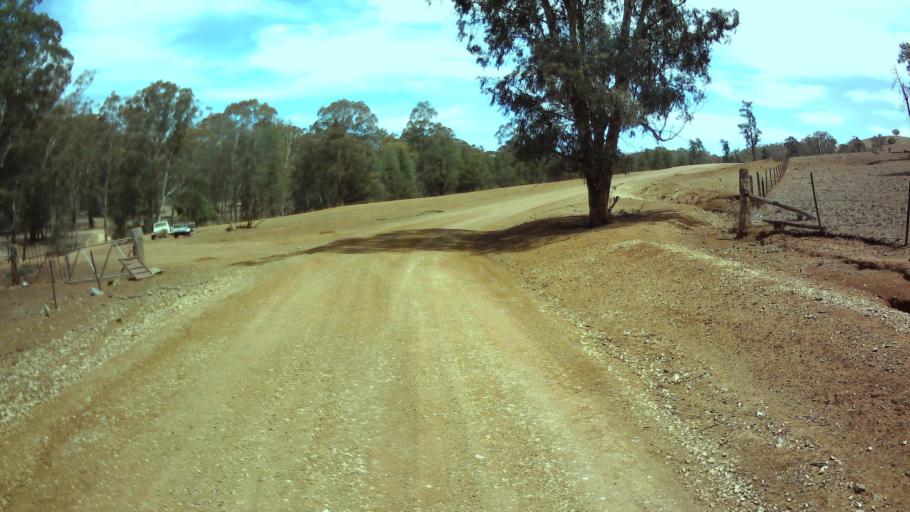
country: AU
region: New South Wales
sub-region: Weddin
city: Grenfell
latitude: -33.7937
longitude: 148.1602
